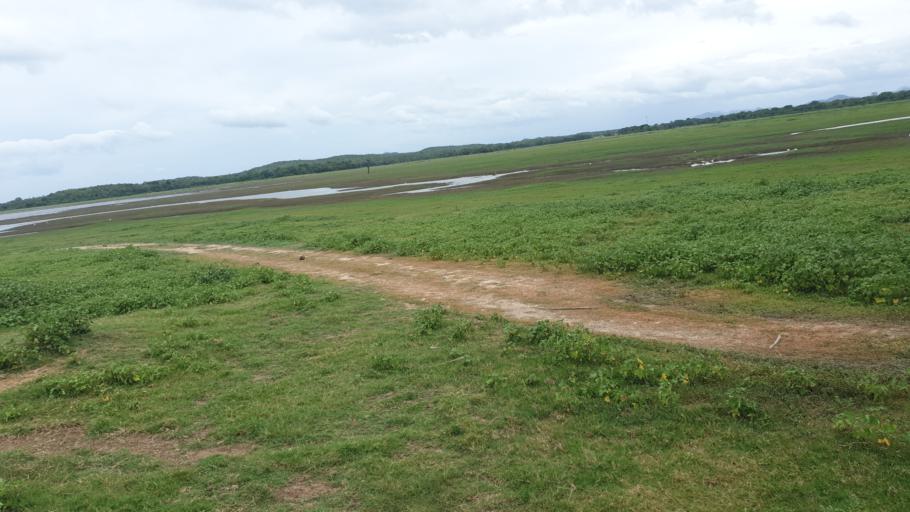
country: LK
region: North Central
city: Polonnaruwa
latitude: 8.1287
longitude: 80.9085
